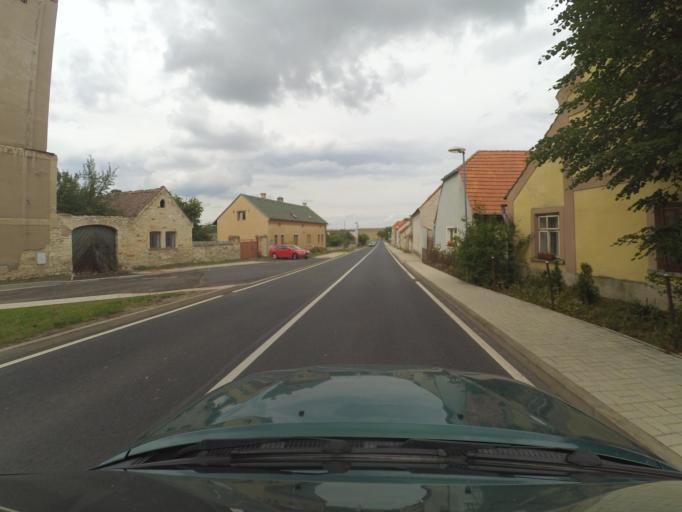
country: CZ
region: Ustecky
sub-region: Okres Louny
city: Louny
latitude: 50.2941
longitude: 13.7817
